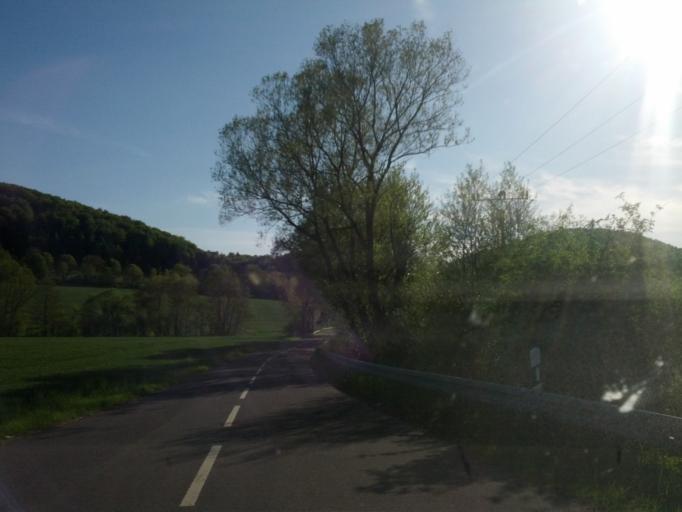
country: DE
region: Thuringia
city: Geismar
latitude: 51.2241
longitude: 10.1867
